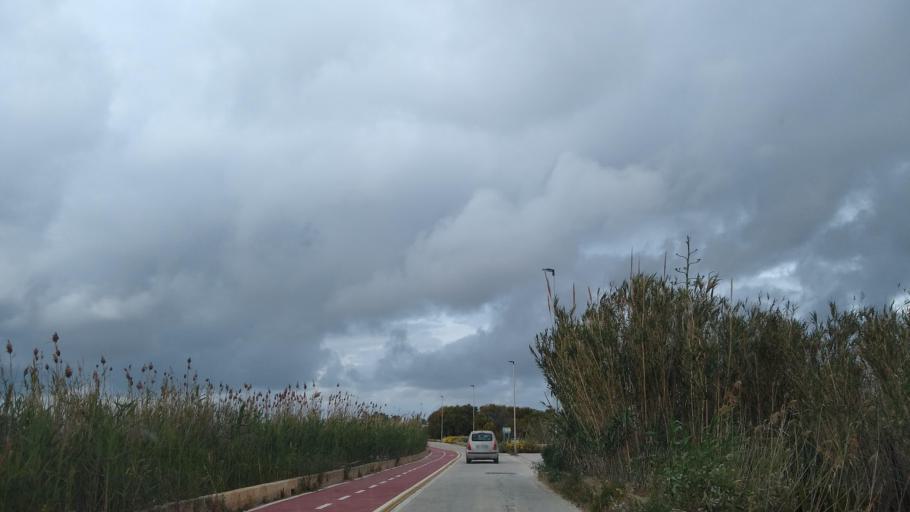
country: IT
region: Sicily
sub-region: Trapani
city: Marsala
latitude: 37.8595
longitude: 12.4850
